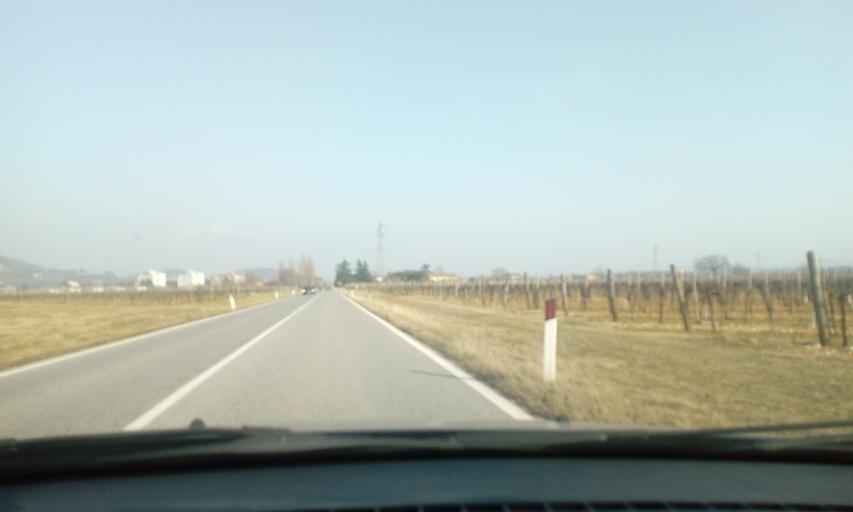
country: IT
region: Friuli Venezia Giulia
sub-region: Provincia di Gorizia
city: Cormons
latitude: 45.9527
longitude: 13.4498
